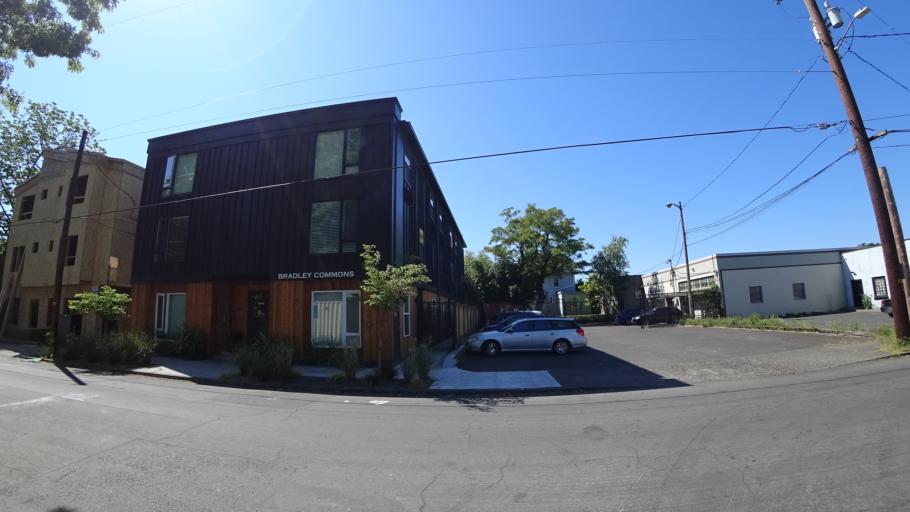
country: US
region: Oregon
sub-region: Multnomah County
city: Portland
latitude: 45.5641
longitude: -122.6608
